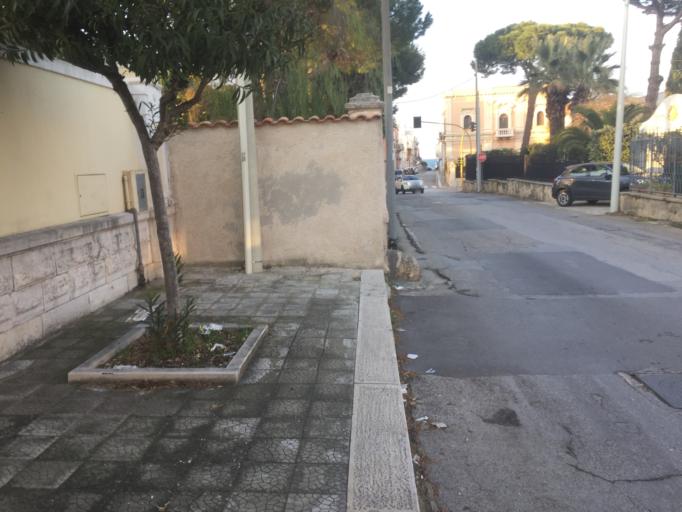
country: IT
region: Apulia
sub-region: Provincia di Bari
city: Parco Scizzo-Parchitello
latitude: 41.0847
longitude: 16.9987
